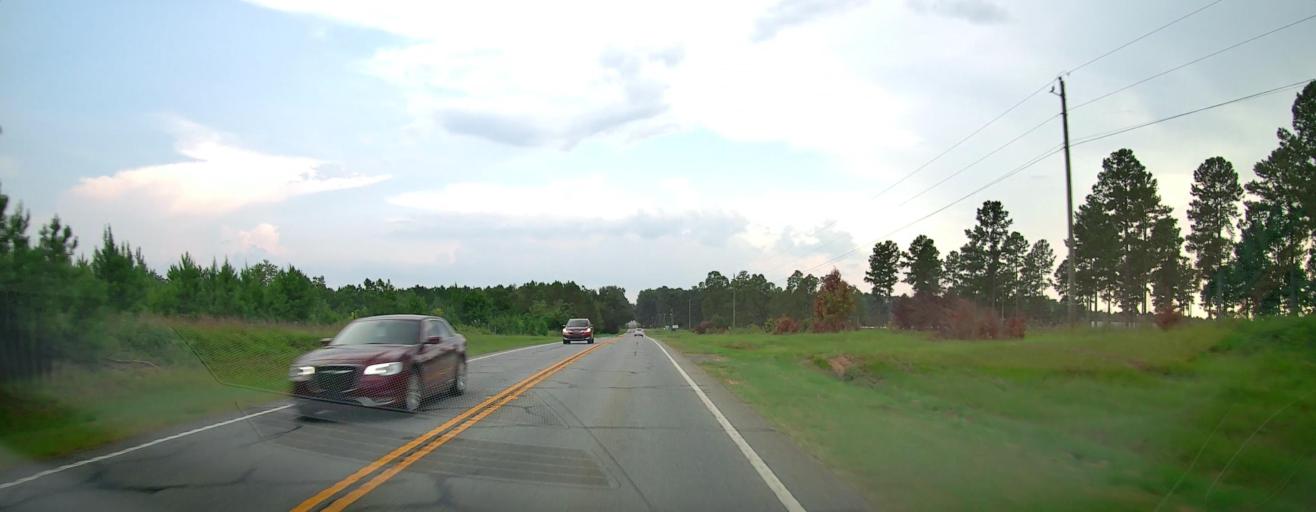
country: US
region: Georgia
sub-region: Laurens County
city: East Dublin
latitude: 32.5893
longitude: -82.8314
